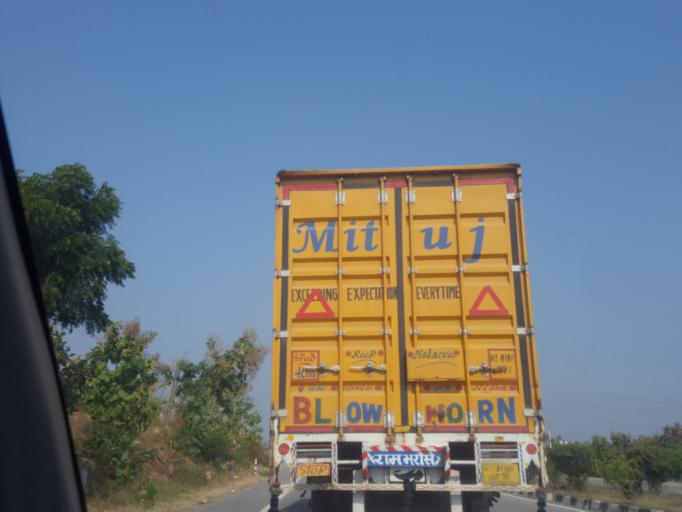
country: IN
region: Telangana
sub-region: Nizamabad District
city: Nizamabad
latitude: 18.5675
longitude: 78.2355
